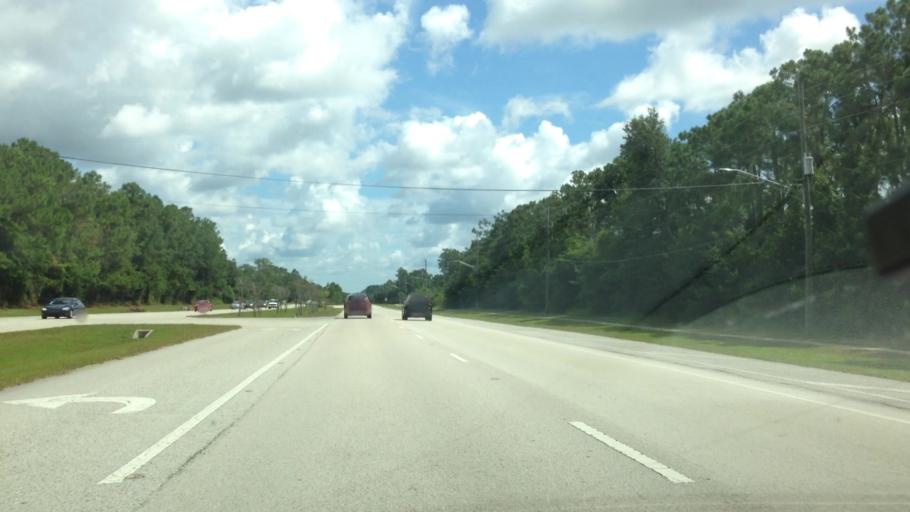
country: US
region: Florida
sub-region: Duval County
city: Jacksonville Beach
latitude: 30.2688
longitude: -81.4642
